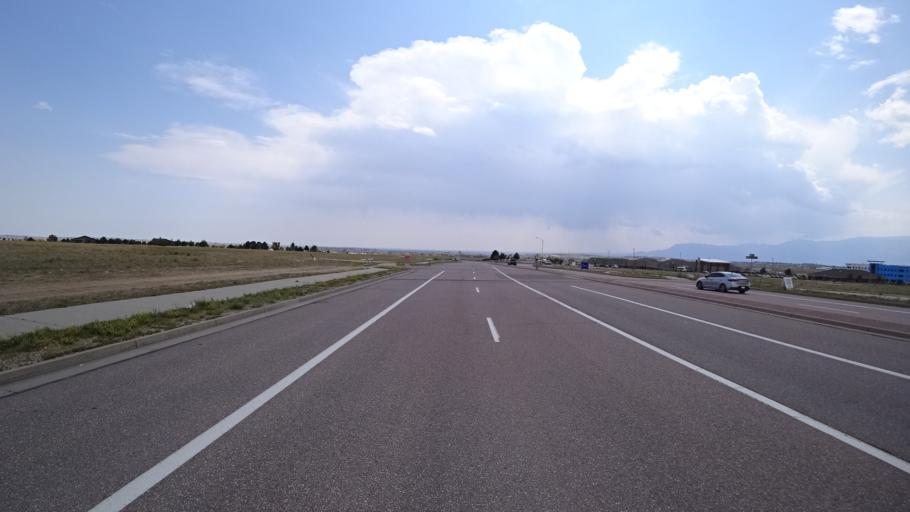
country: US
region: Colorado
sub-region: El Paso County
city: Black Forest
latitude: 38.9397
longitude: -104.7110
